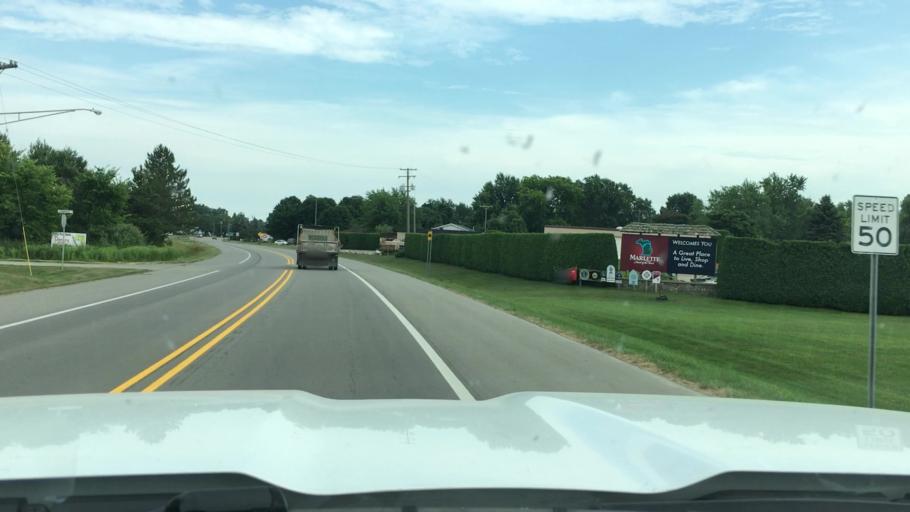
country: US
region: Michigan
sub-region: Sanilac County
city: Marlette
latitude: 43.3380
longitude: -83.0838
